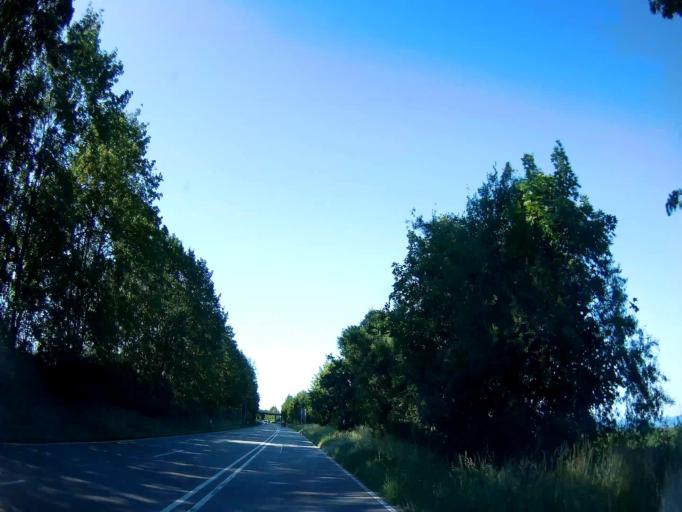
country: DE
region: Bavaria
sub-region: Lower Bavaria
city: Alterhofen
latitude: 48.8485
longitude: 12.6299
